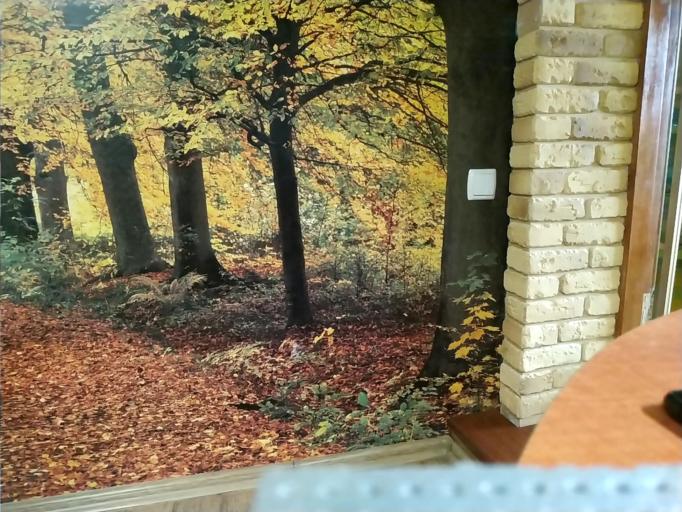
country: RU
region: Vladimir
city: Bavleny
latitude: 56.3671
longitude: 39.5586
